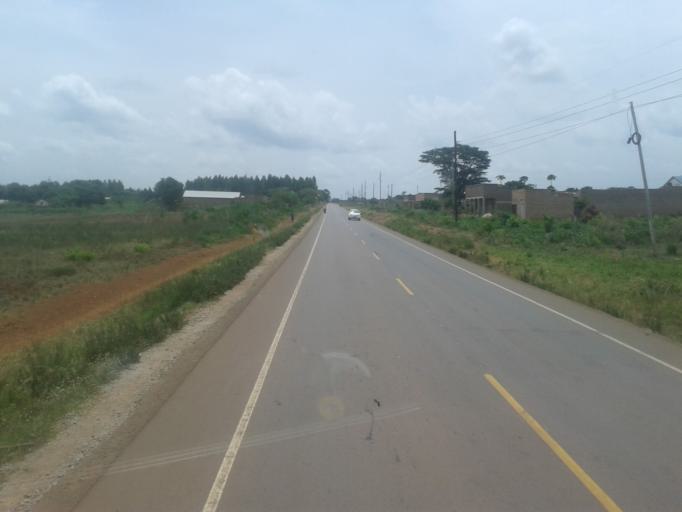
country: UG
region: Western Region
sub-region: Kiryandongo District
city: Kiryandongo
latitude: 1.7930
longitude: 32.0131
